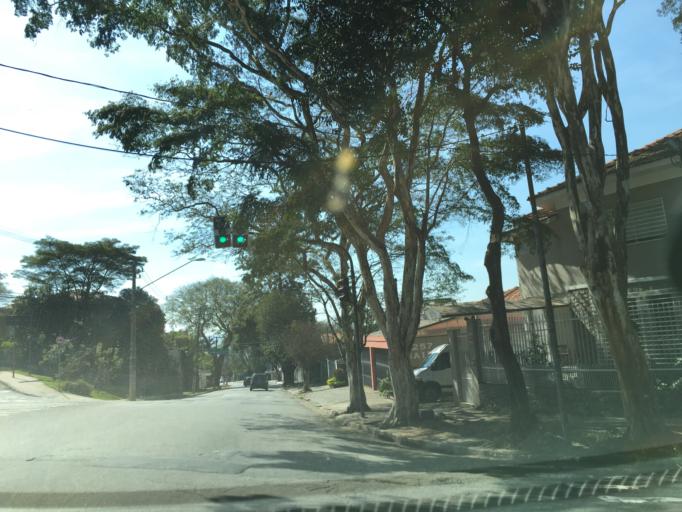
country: BR
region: Sao Paulo
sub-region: Sao Paulo
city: Sao Paulo
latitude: -23.5335
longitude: -46.7128
